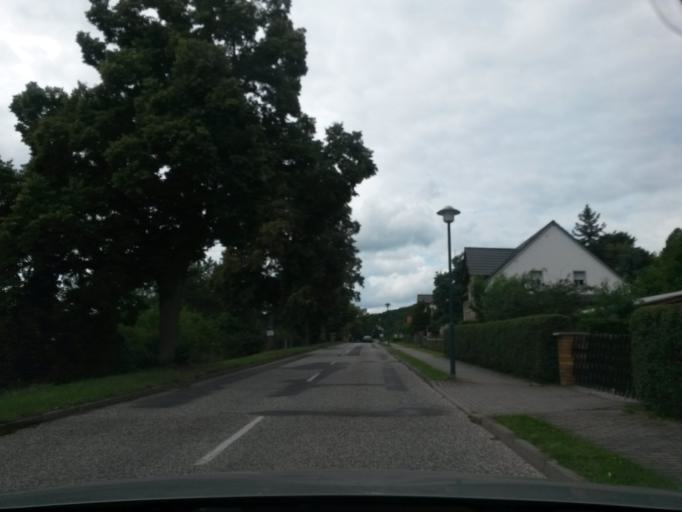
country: DE
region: Brandenburg
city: Liepe
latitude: 52.8589
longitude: 13.9555
